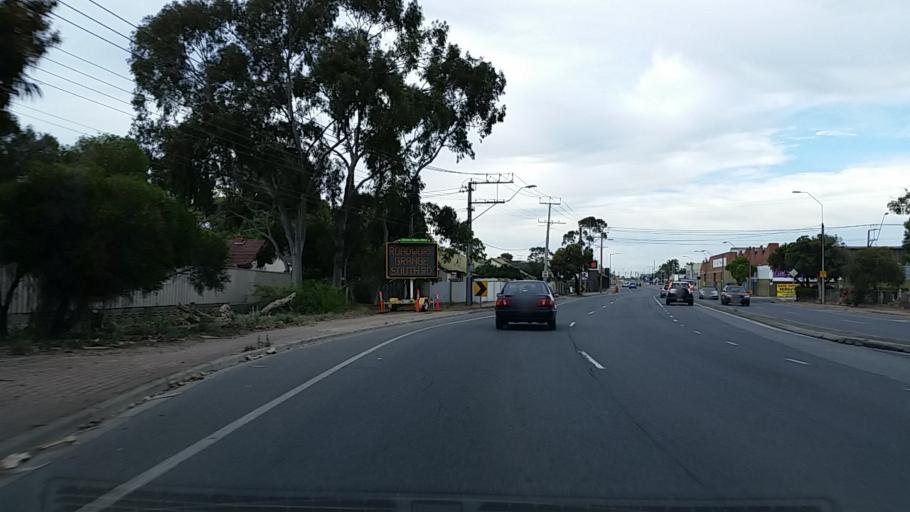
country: AU
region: South Australia
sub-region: City of West Torrens
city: Thebarton
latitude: -34.9118
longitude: 138.5645
